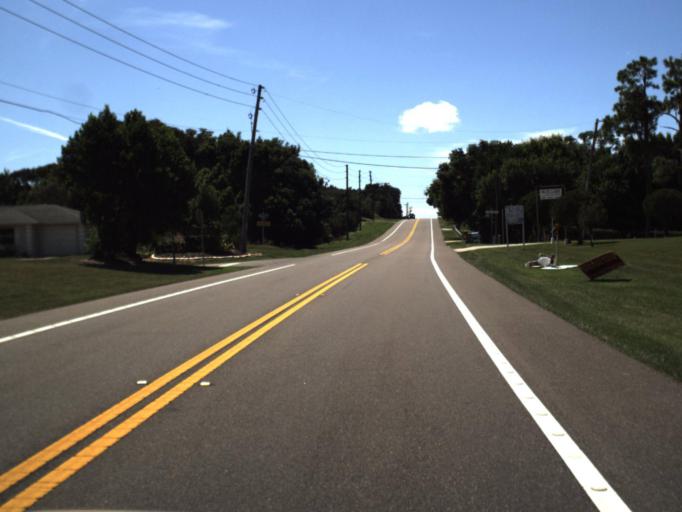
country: US
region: Florida
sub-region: Polk County
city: Crooked Lake Park
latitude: 27.8521
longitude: -81.5722
